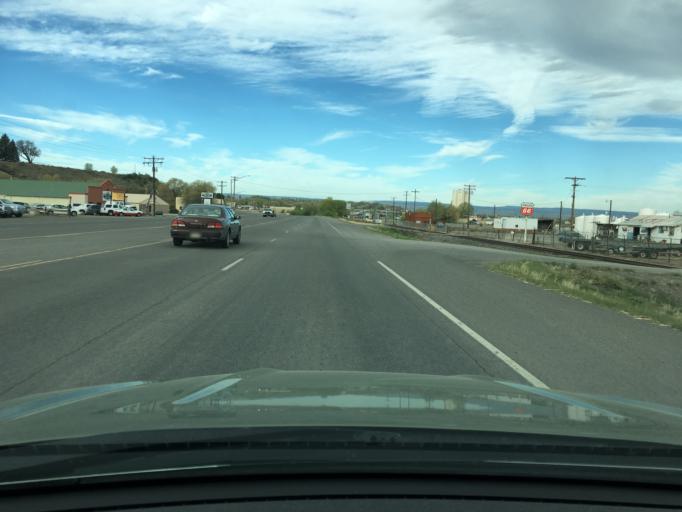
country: US
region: Colorado
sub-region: Delta County
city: Delta
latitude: 38.7492
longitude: -108.0628
